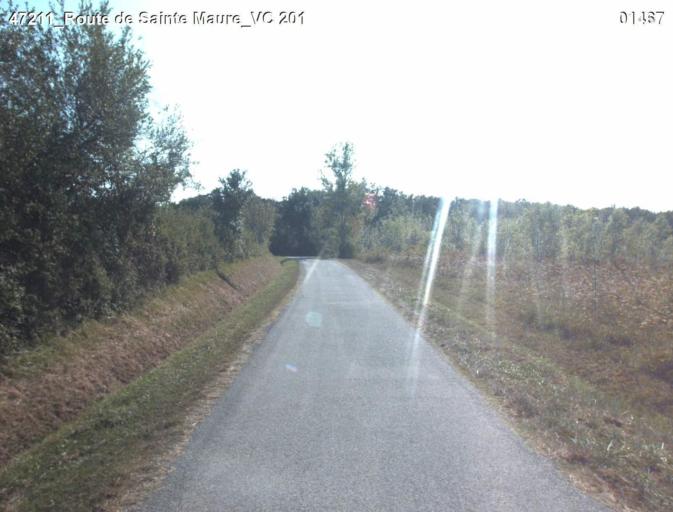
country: FR
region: Aquitaine
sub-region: Departement du Lot-et-Garonne
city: Mezin
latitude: 44.0318
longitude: 0.1876
